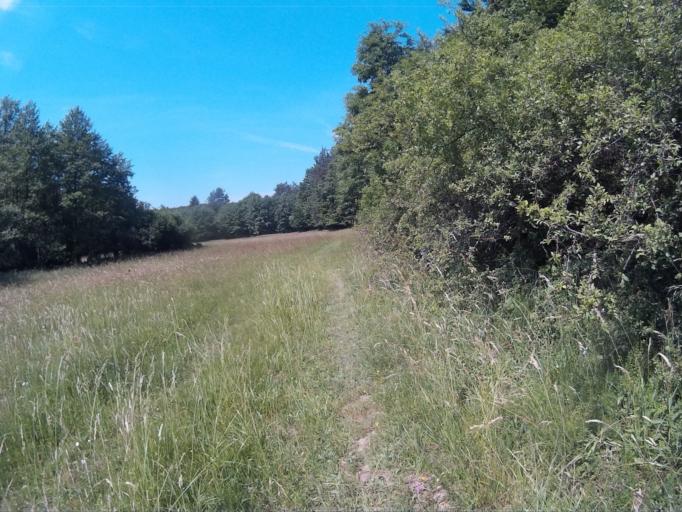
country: SI
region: Hodos-Hodos
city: Hodos
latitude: 46.8950
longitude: 16.4335
